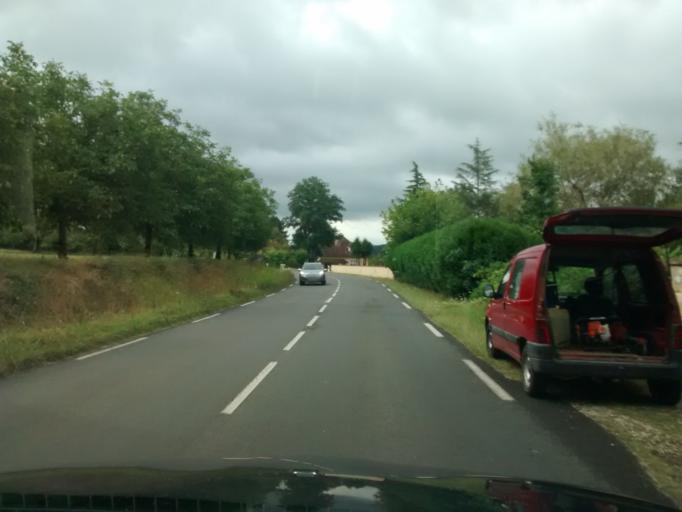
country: FR
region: Aquitaine
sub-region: Departement de la Dordogne
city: Carsac-Aillac
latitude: 44.8300
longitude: 1.2775
